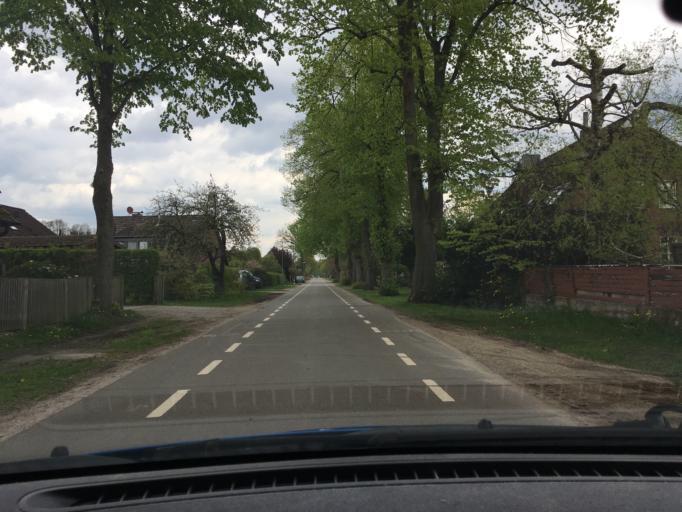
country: DE
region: Lower Saxony
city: Radbruch
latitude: 53.3034
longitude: 10.2740
